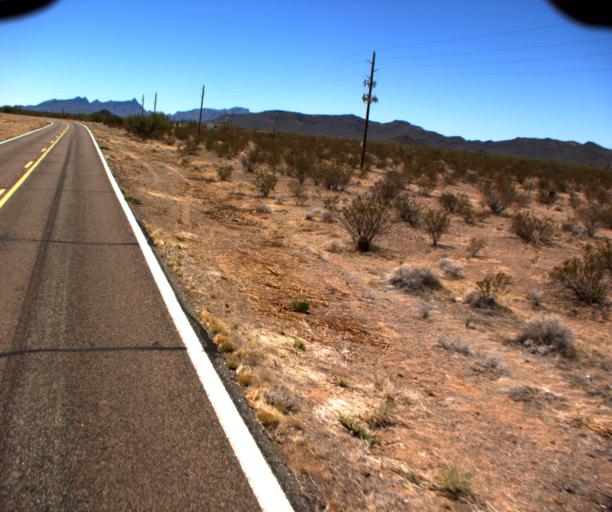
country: US
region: Arizona
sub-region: Pima County
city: Ajo
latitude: 32.2463
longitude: -112.7288
